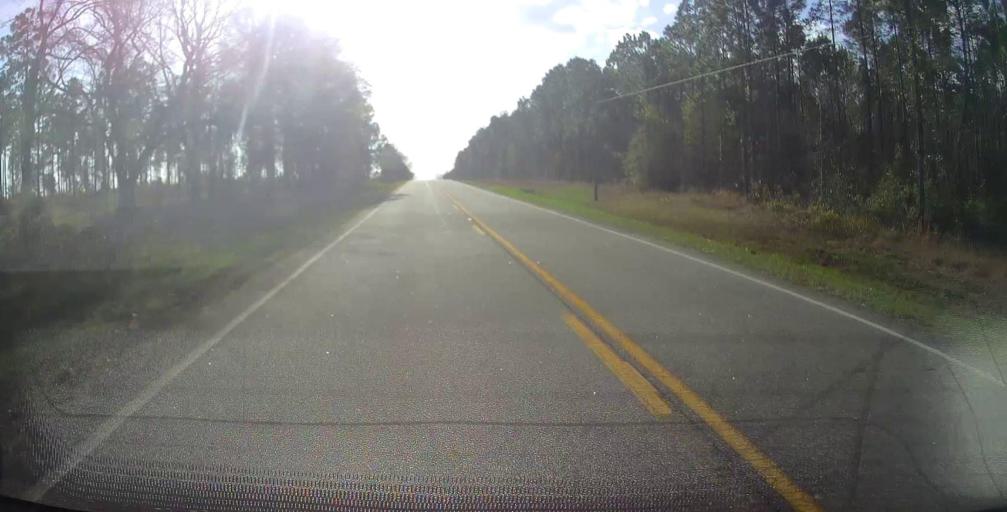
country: US
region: Georgia
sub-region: Wheeler County
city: Alamo
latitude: 32.1695
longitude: -82.6969
